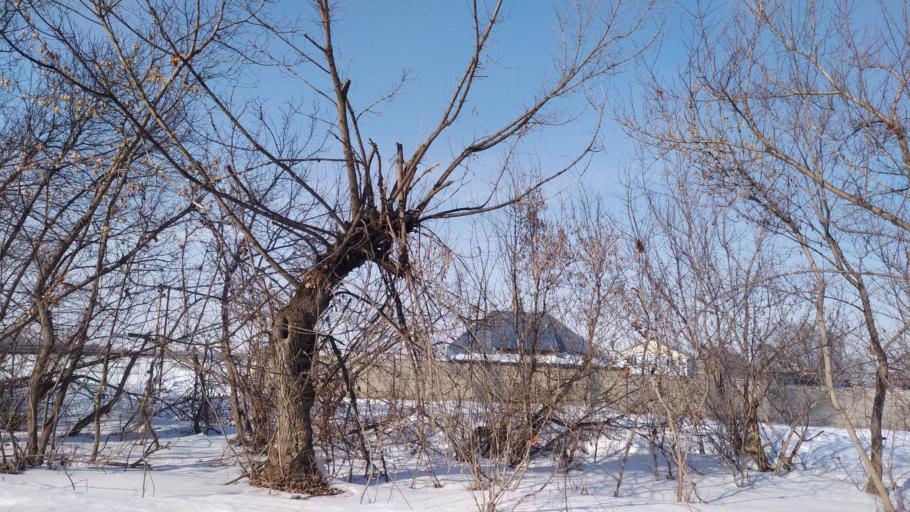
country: KZ
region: Almaty Oblysy
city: Burunday
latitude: 43.2421
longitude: 76.4285
